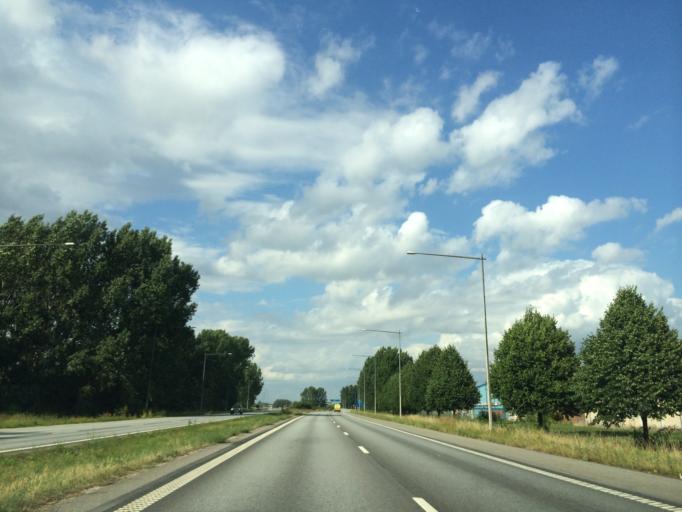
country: SE
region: Skane
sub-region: Burlovs Kommun
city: Arloev
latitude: 55.6343
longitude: 13.0564
